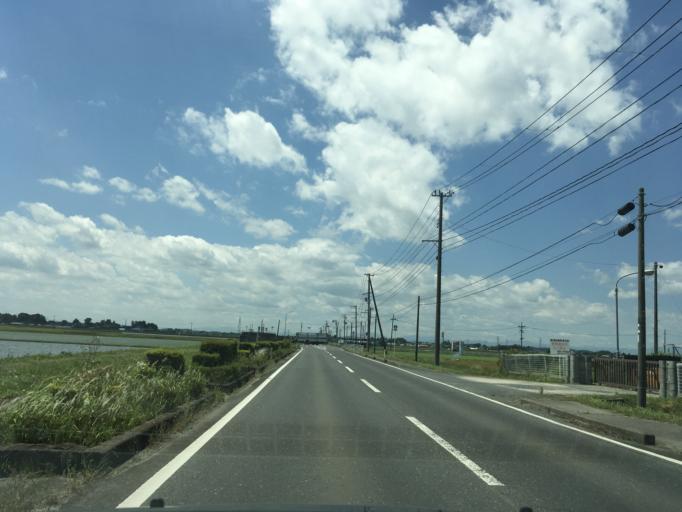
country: JP
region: Miyagi
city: Wakuya
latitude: 38.6778
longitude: 141.2343
